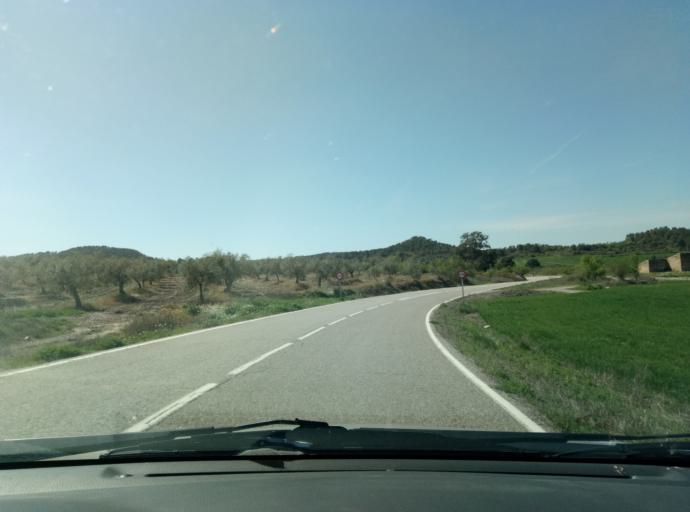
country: ES
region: Catalonia
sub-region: Provincia de Lleida
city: Vallbona de les Monges
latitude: 41.5255
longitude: 1.0329
